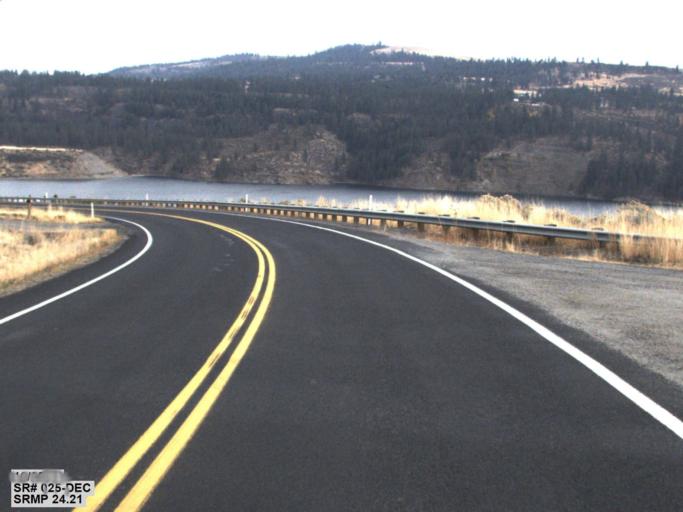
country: US
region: Washington
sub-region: Lincoln County
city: Davenport
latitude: 47.9063
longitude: -118.3333
